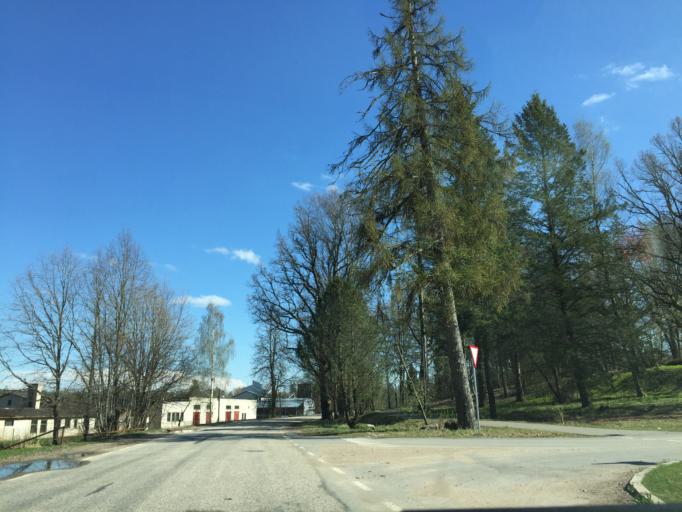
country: EE
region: Valgamaa
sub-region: Valga linn
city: Valga
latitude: 57.8548
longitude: 26.1183
